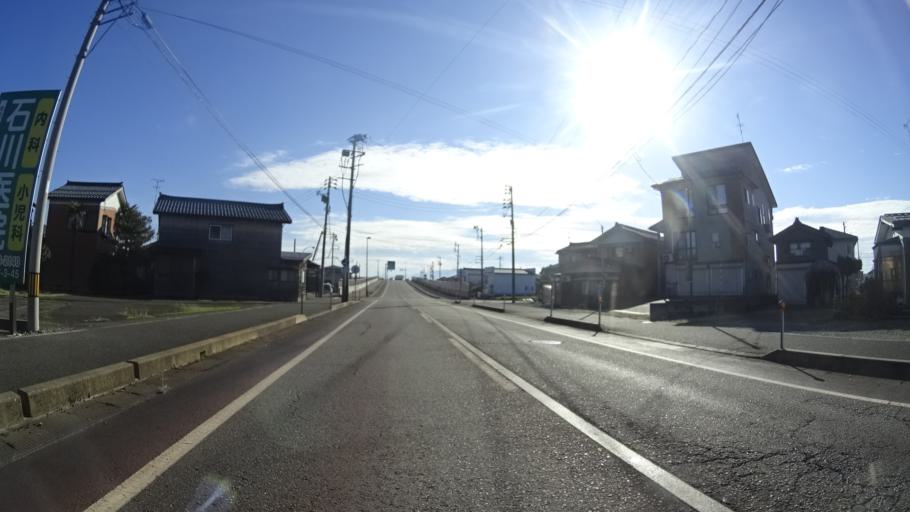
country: JP
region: Niigata
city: Mitsuke
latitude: 37.5468
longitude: 138.8789
